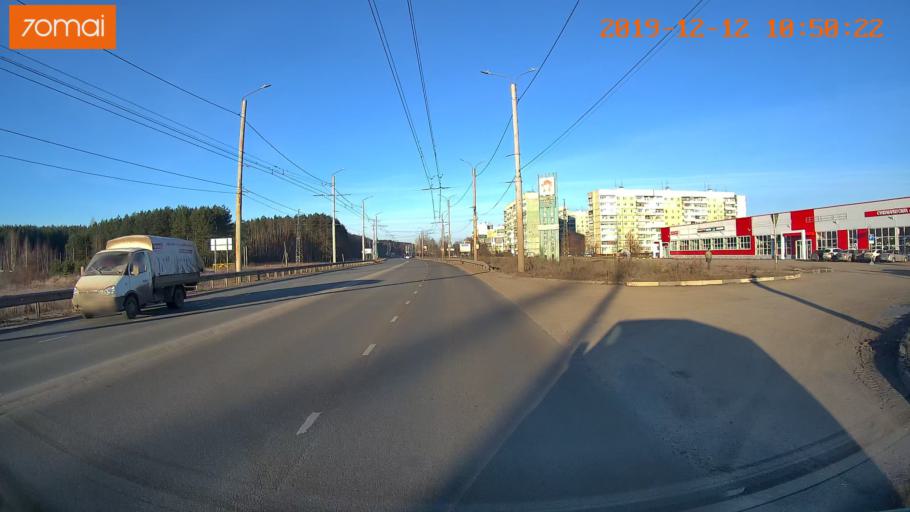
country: RU
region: Ivanovo
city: Kokhma
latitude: 56.9467
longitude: 41.0549
